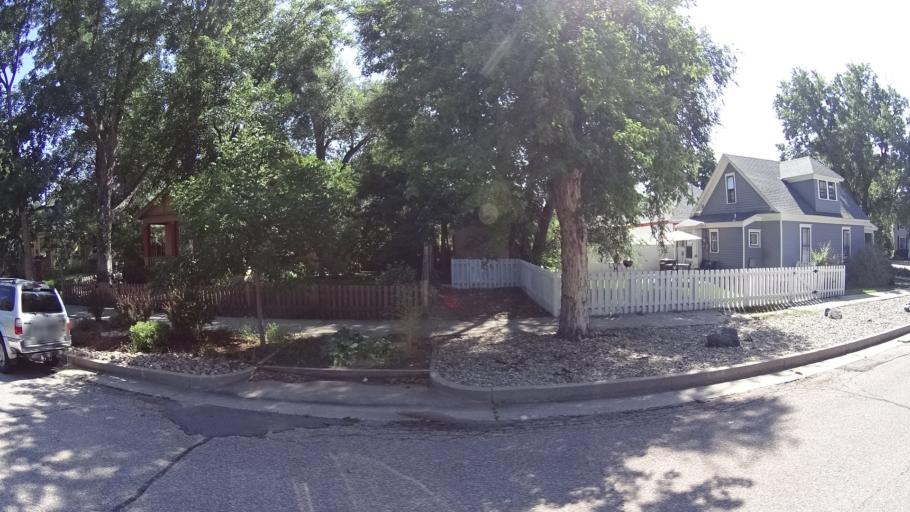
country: US
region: Colorado
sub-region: El Paso County
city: Colorado Springs
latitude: 38.8521
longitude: -104.8154
